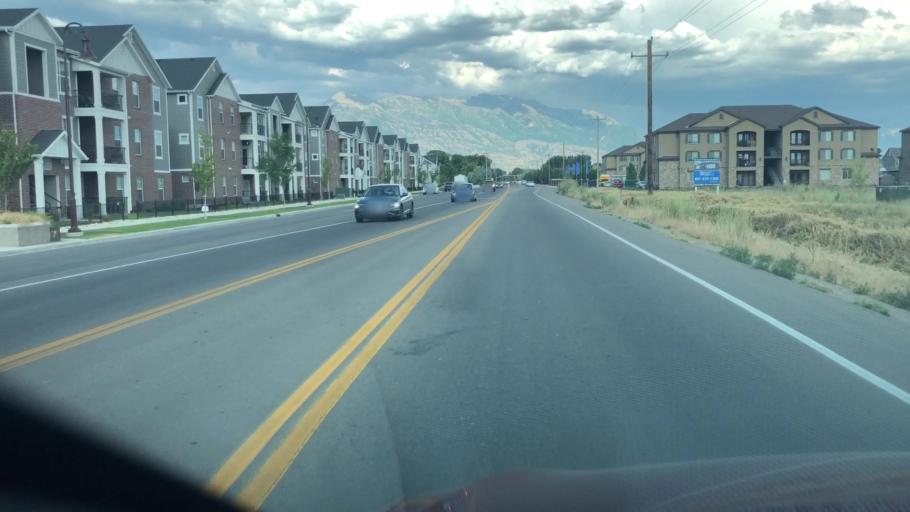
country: US
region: Utah
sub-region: Utah County
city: Lehi
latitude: 40.3873
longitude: -111.8851
